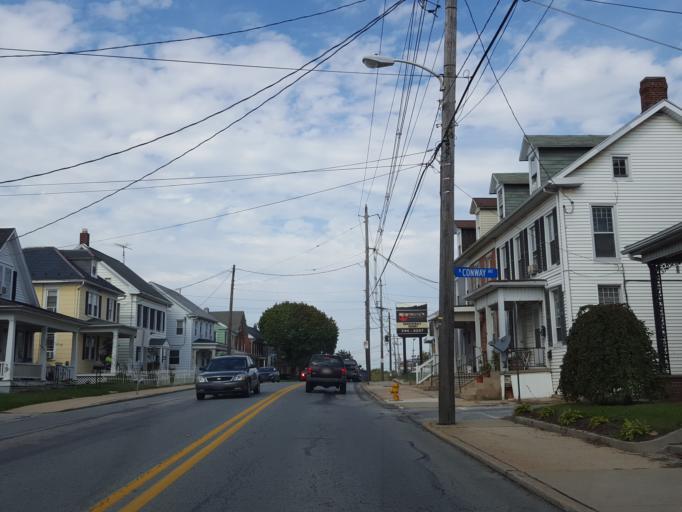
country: US
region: Pennsylvania
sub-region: York County
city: Dallastown
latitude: 39.9040
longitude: -76.6511
